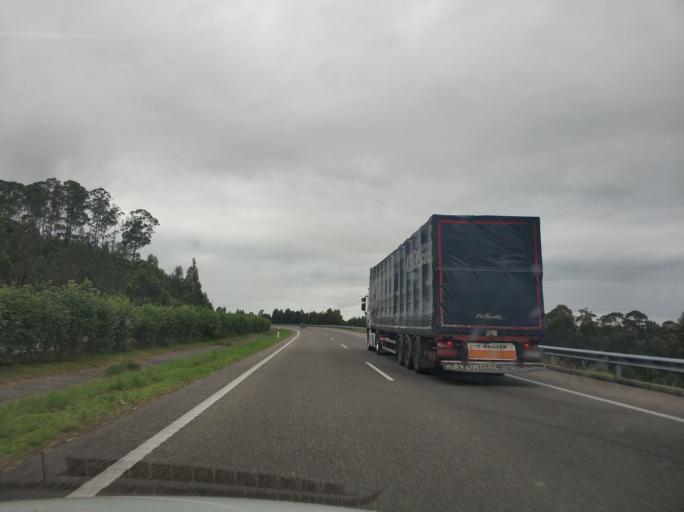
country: ES
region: Galicia
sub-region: Provincia de Lugo
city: Ribadeo
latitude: 43.5329
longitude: -7.1079
